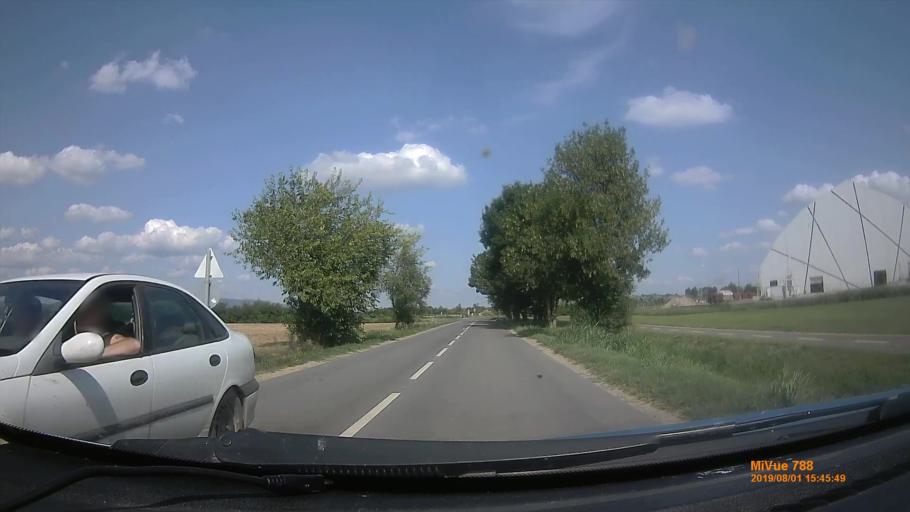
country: HU
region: Baranya
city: Szentlorinc
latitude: 46.0182
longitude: 17.9805
